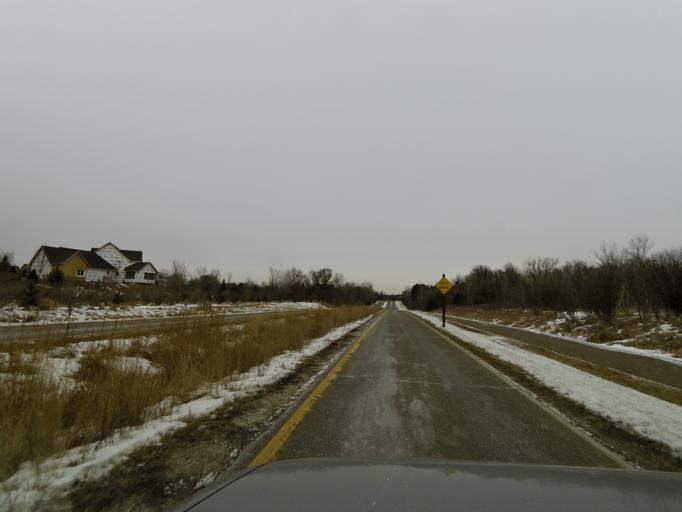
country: US
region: Minnesota
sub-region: Washington County
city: Lake Elmo
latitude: 44.9669
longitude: -92.9033
